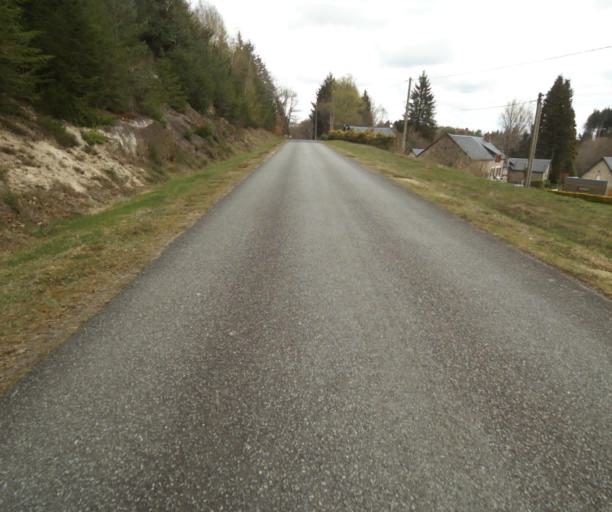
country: FR
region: Limousin
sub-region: Departement de la Correze
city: Correze
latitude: 45.3605
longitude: 1.9270
